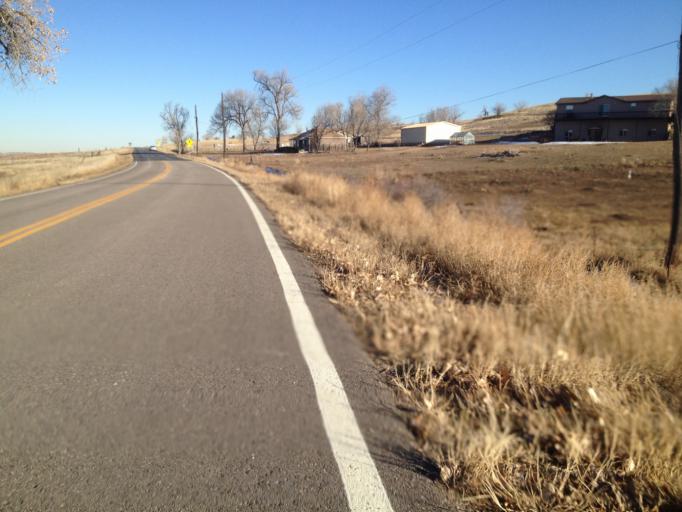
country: US
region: Colorado
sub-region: Boulder County
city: Louisville
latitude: 39.9761
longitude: -105.1160
